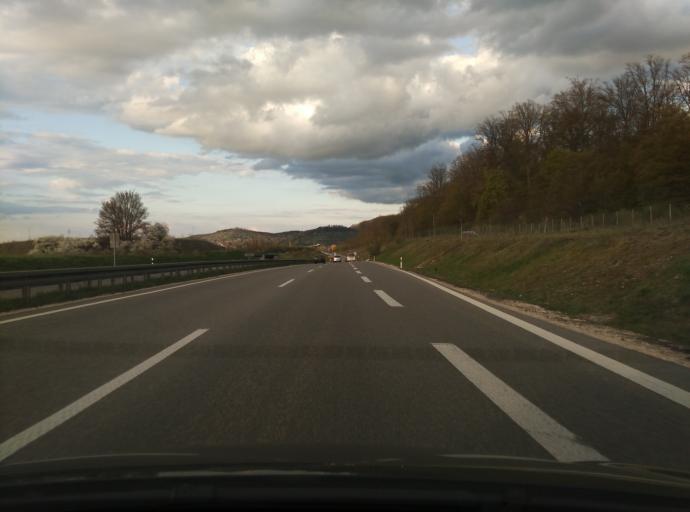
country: DE
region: Baden-Wuerttemberg
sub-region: Tuebingen Region
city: Metzingen
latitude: 48.5252
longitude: 9.2572
